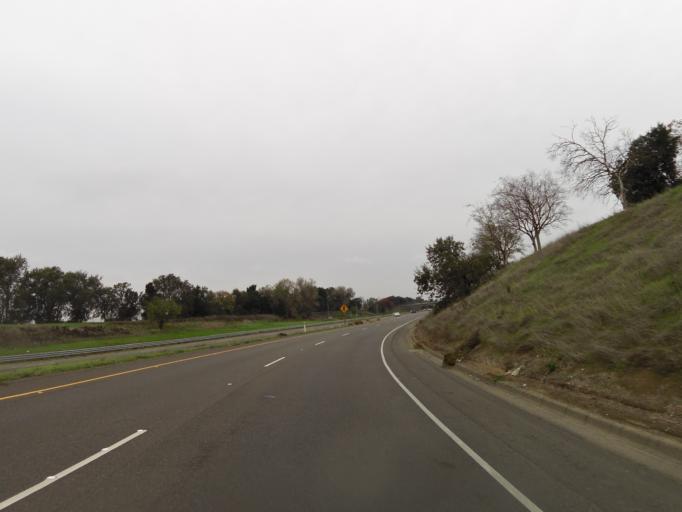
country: US
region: California
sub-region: Yolo County
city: Davis
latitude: 38.5274
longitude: -121.7683
